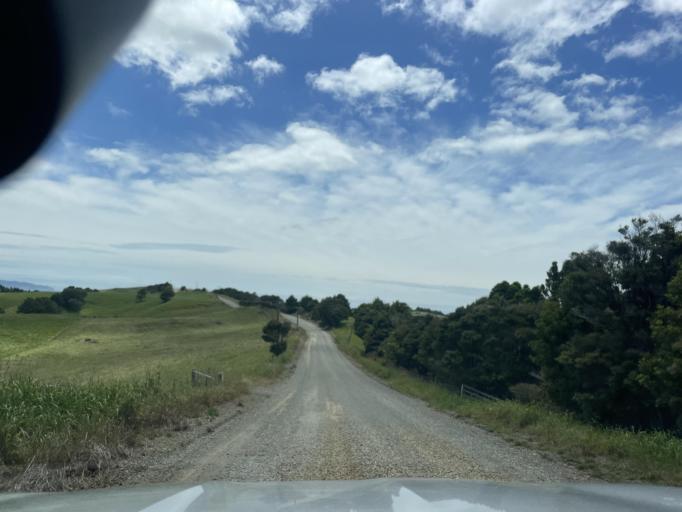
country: NZ
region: Auckland
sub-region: Auckland
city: Wellsford
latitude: -36.1614
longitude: 174.5331
